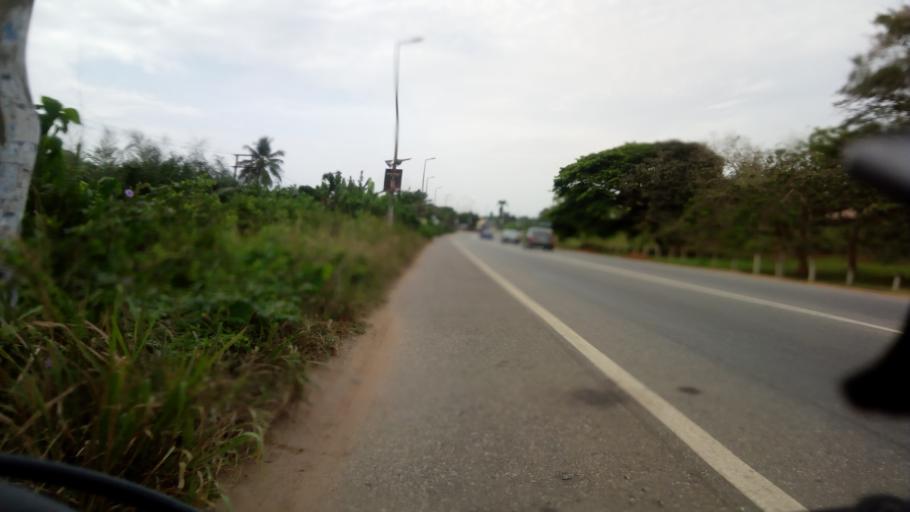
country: GH
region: Central
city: Cape Coast
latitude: 5.1085
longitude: -1.2790
